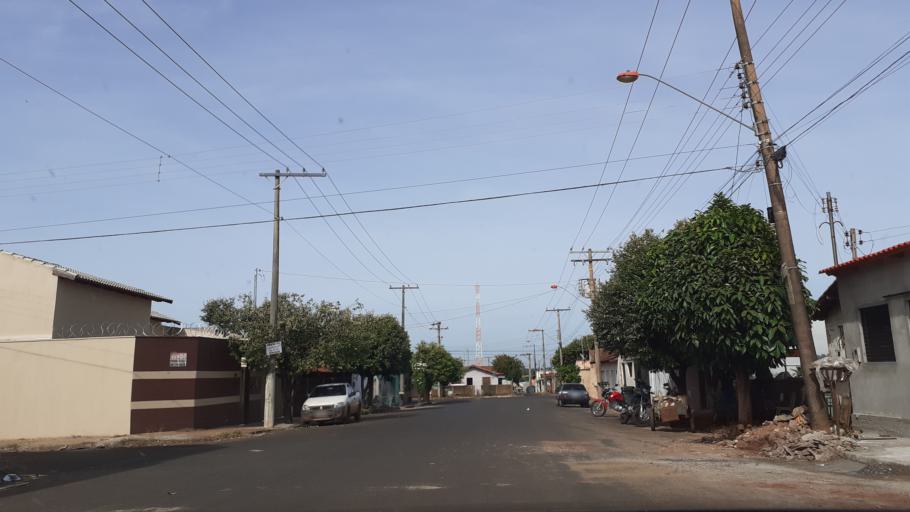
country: BR
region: Goias
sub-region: Itumbiara
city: Itumbiara
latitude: -18.4158
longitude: -49.2365
